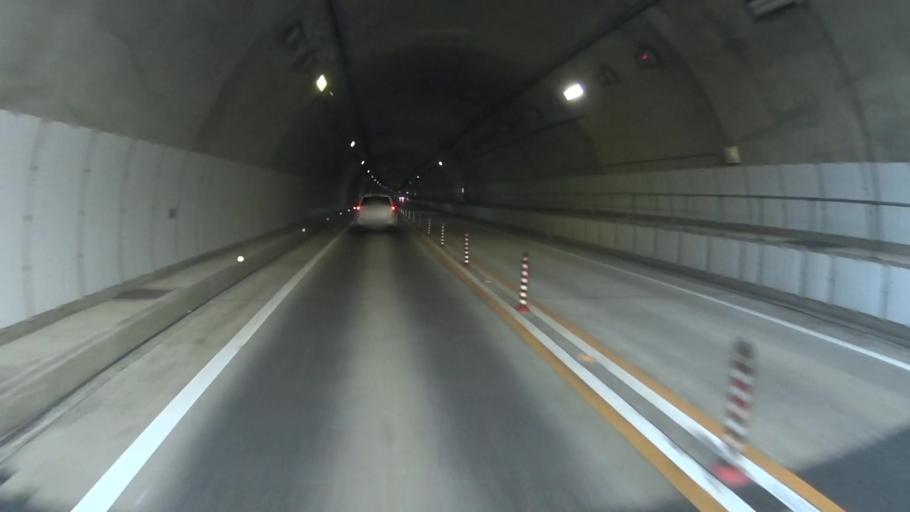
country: JP
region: Kyoto
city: Ayabe
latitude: 35.3321
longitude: 135.3115
